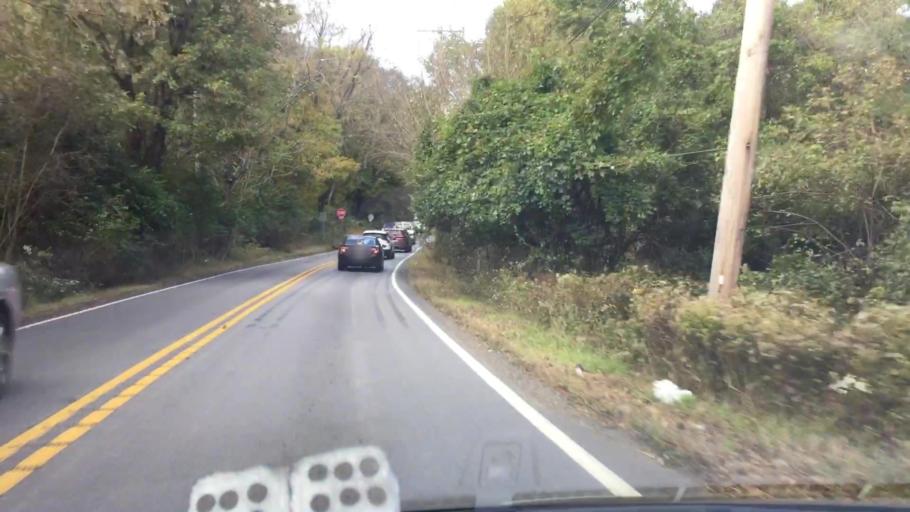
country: US
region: Pennsylvania
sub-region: Delaware County
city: Lima
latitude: 39.9591
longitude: -75.4323
